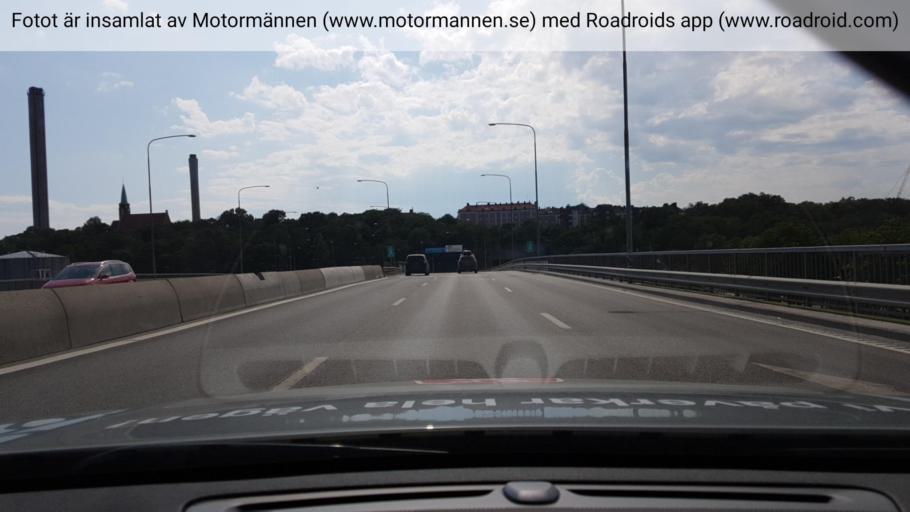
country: SE
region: Stockholm
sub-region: Lidingo
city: Lidingoe
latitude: 59.3594
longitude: 18.1070
